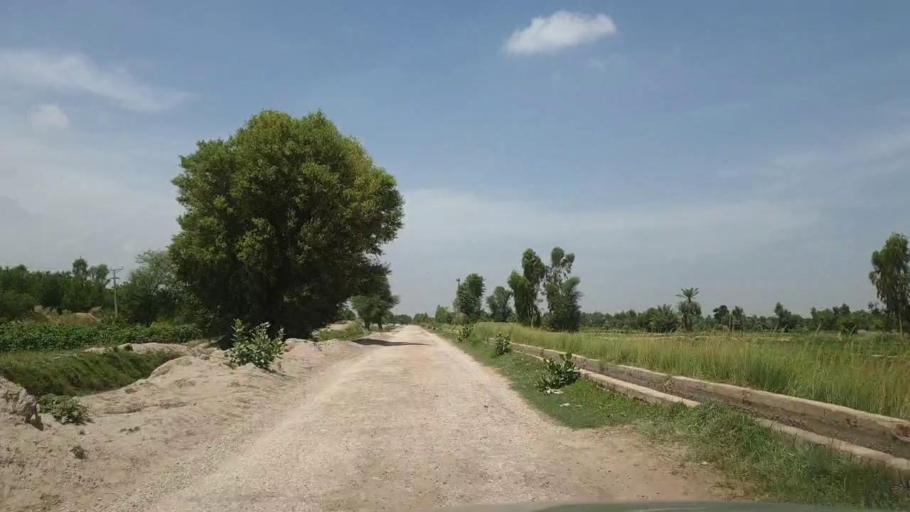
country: PK
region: Sindh
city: Kot Diji
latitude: 27.1354
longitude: 69.0376
